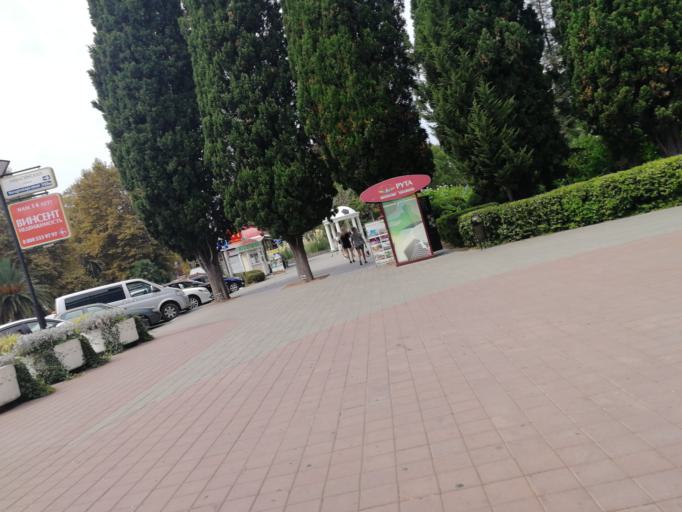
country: RU
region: Krasnodarskiy
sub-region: Sochi City
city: Sochi
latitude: 43.5834
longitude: 39.7217
